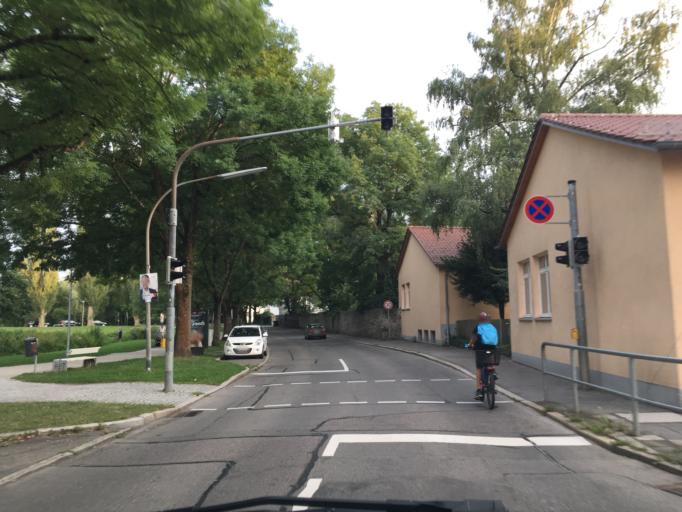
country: DE
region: Baden-Wuerttemberg
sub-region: Regierungsbezirk Stuttgart
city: Sindelfingen
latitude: 48.7130
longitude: 9.0021
